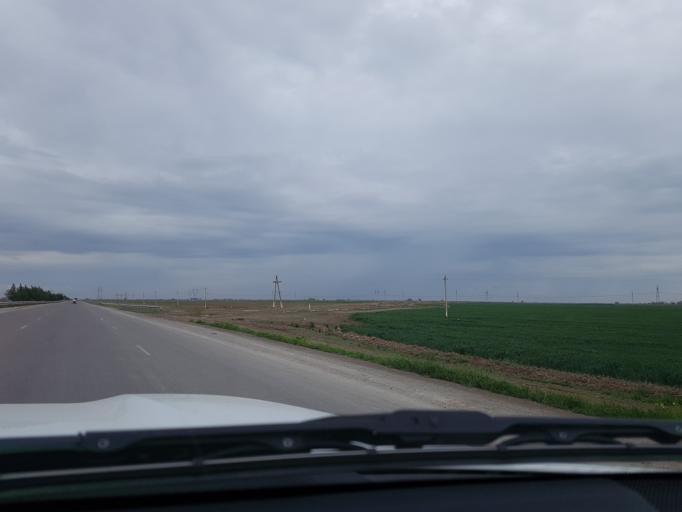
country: TM
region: Mary
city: Bayramaly
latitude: 37.6219
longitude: 62.0978
